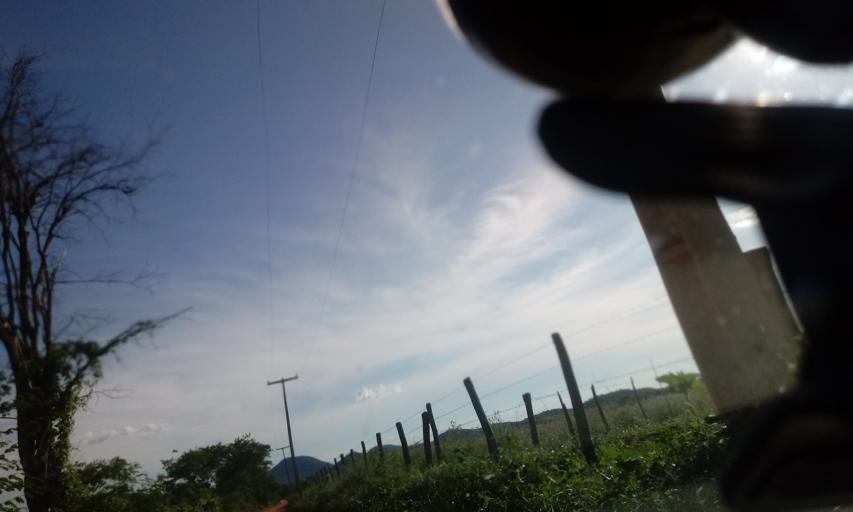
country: BR
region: Bahia
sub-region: Riacho De Santana
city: Riacho de Santana
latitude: -13.8568
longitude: -42.7775
